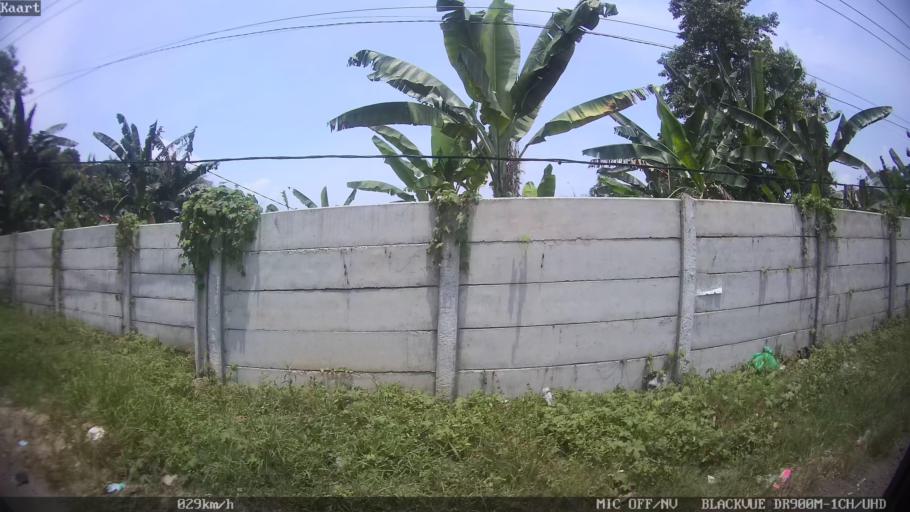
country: ID
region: Lampung
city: Bandarlampung
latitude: -5.4347
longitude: 105.2489
